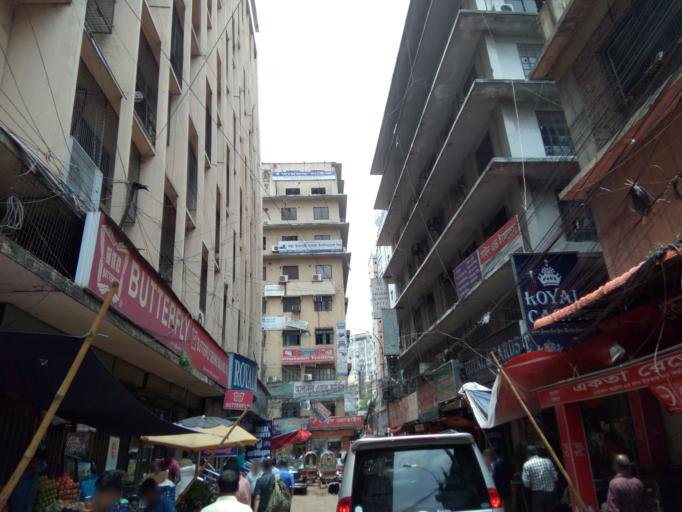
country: BD
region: Dhaka
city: Paltan
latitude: 23.7304
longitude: 90.4117
